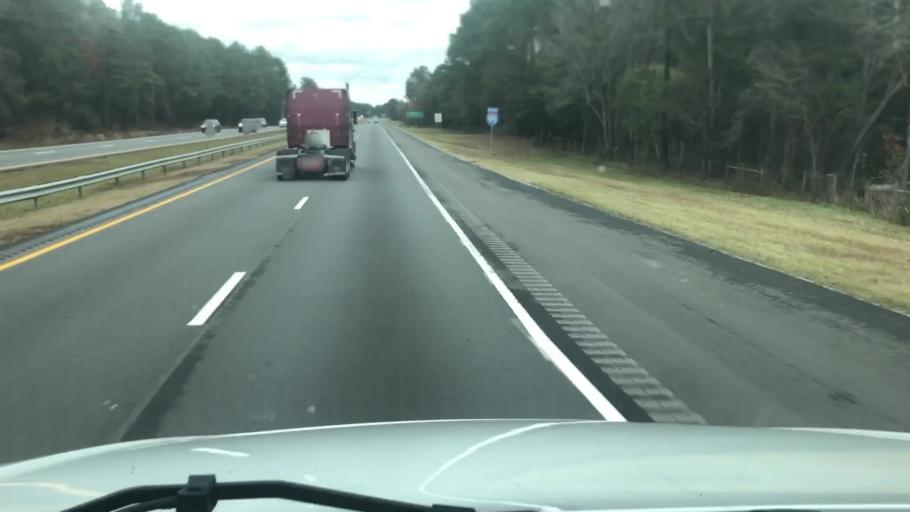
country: US
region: North Carolina
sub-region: Cumberland County
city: Eastover
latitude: 35.1016
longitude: -78.7733
